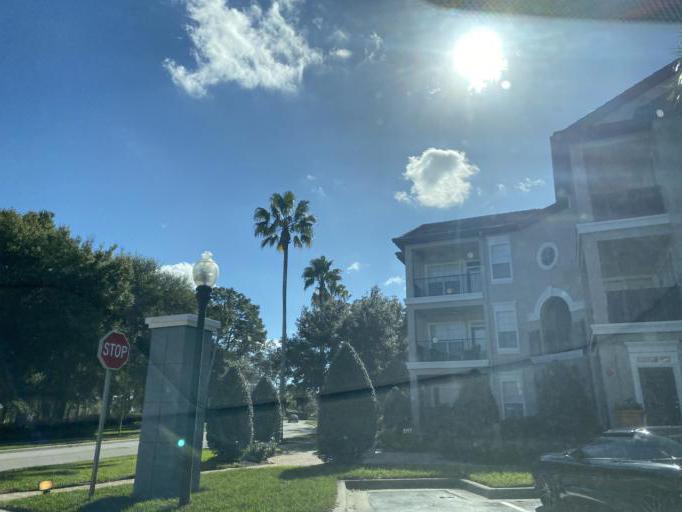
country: US
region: Florida
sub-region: Seminole County
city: Heathrow
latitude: 28.7889
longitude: -81.3549
